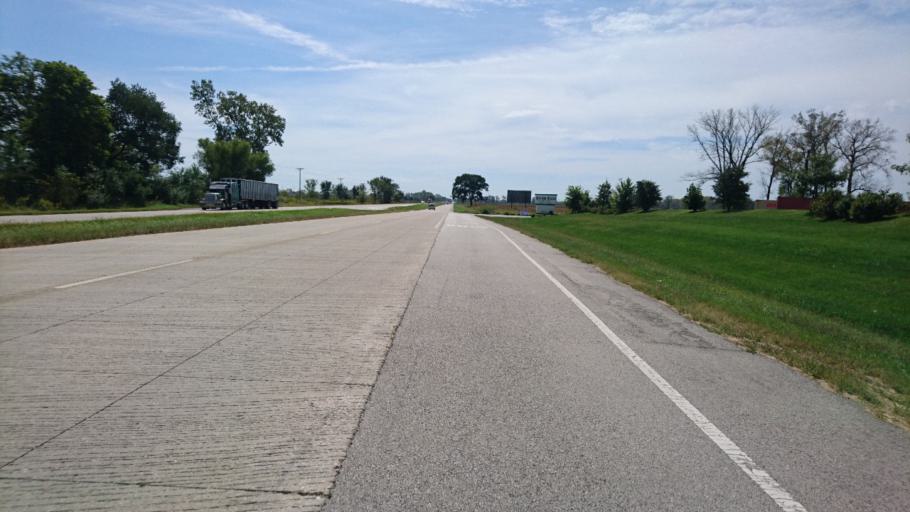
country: US
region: Illinois
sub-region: Will County
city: Wilmington
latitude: 41.3502
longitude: -88.1337
